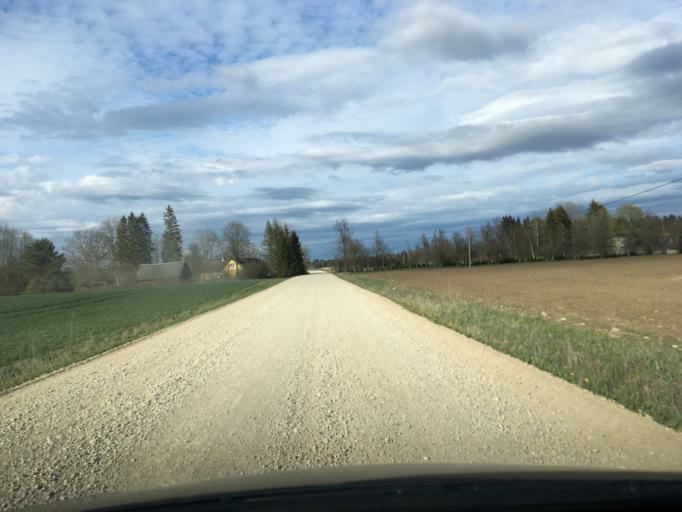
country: EE
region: Raplamaa
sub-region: Maerjamaa vald
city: Marjamaa
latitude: 58.9762
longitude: 24.3532
